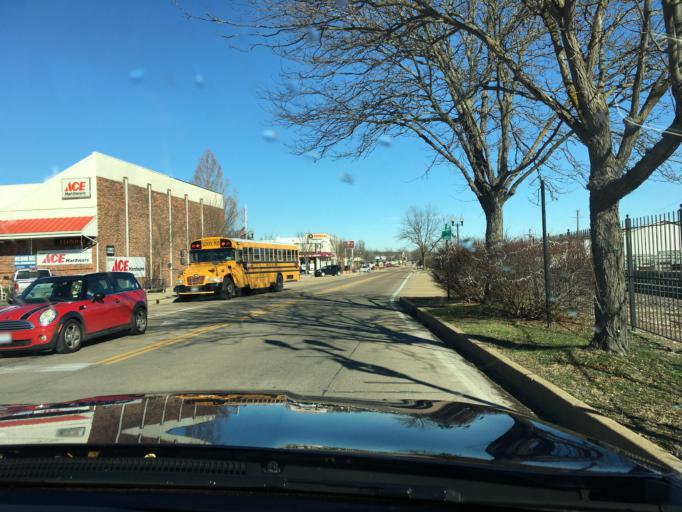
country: US
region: Missouri
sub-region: Jefferson County
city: De Soto
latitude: 38.1400
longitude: -90.5533
